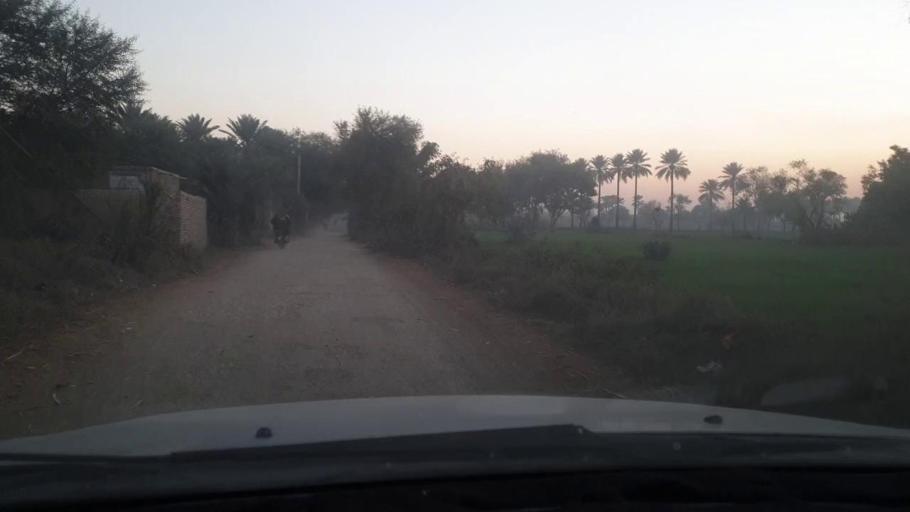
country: PK
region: Sindh
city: Ghotki
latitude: 28.0066
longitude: 69.3379
